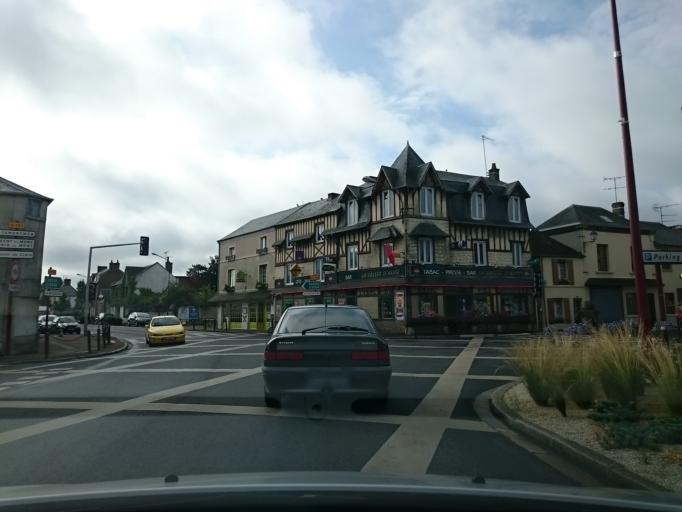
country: FR
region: Lower Normandy
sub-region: Departement du Calvados
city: Cambremer
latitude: 49.1188
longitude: 0.0148
